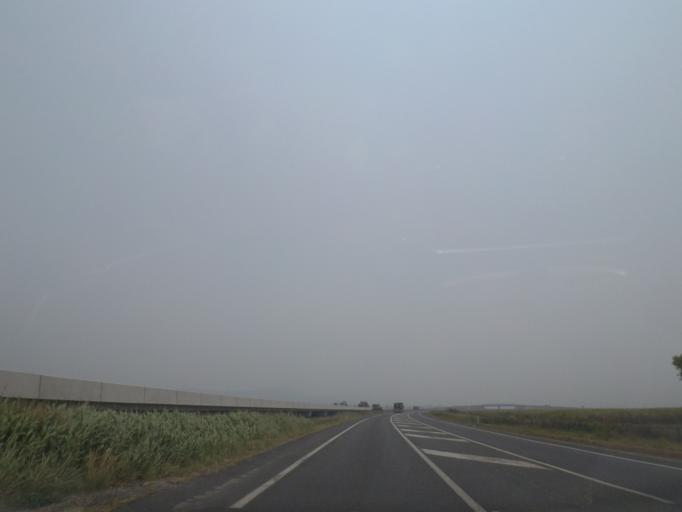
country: AU
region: New South Wales
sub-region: Clarence Valley
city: Maclean
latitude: -29.3997
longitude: 153.2403
